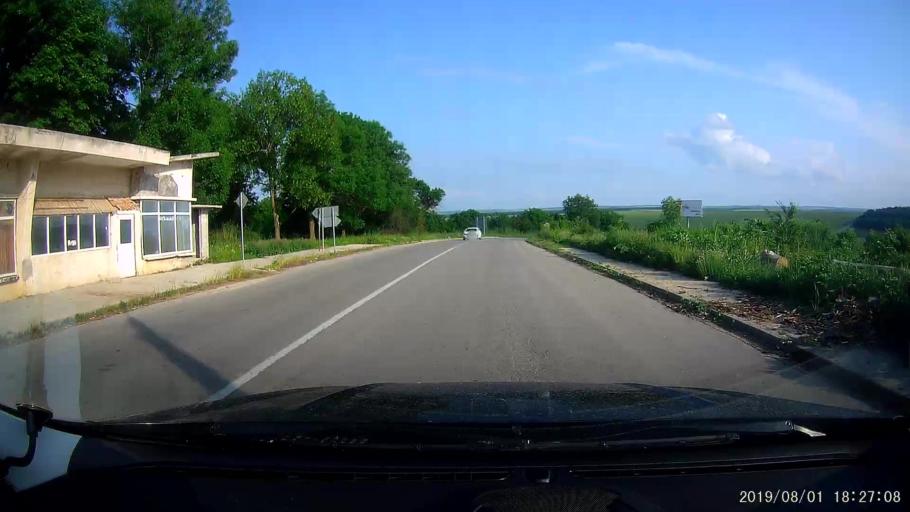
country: BG
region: Shumen
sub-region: Obshtina Venets
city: Venets
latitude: 43.5916
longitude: 26.9832
